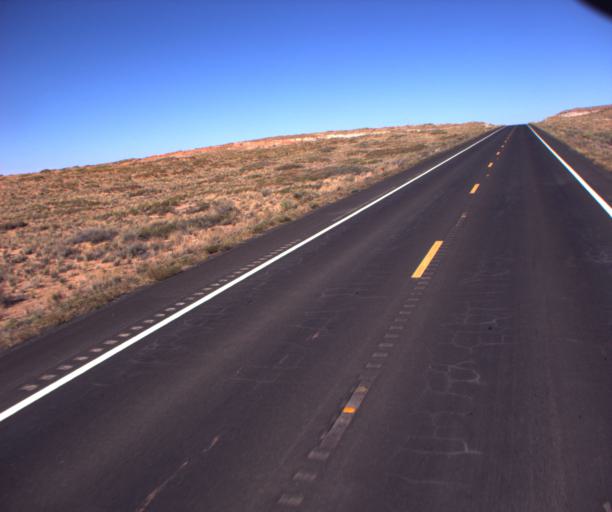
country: US
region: Arizona
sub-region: Coconino County
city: Tuba City
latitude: 36.2209
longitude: -111.0406
